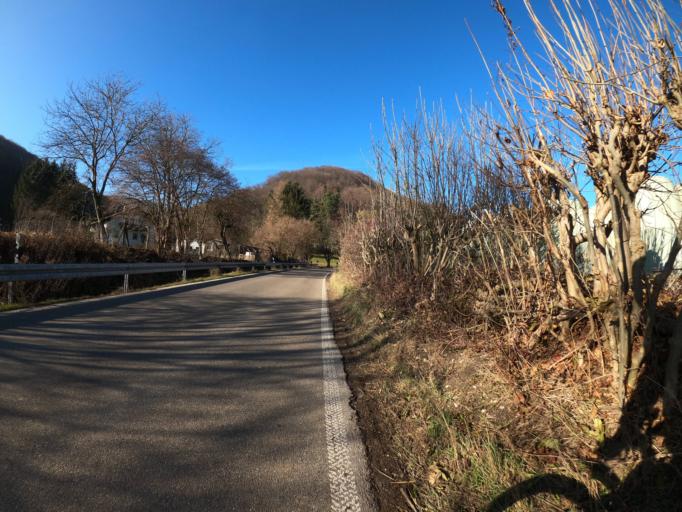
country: DE
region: Baden-Wuerttemberg
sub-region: Regierungsbezirk Stuttgart
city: Bad Ditzenbach
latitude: 48.6075
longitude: 9.6799
